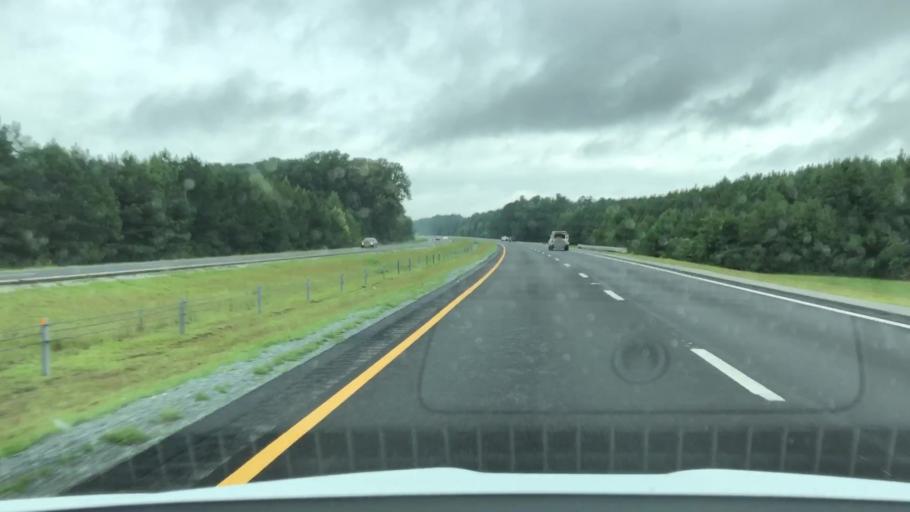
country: US
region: North Carolina
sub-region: Wayne County
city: Fremont
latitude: 35.4737
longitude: -77.9871
